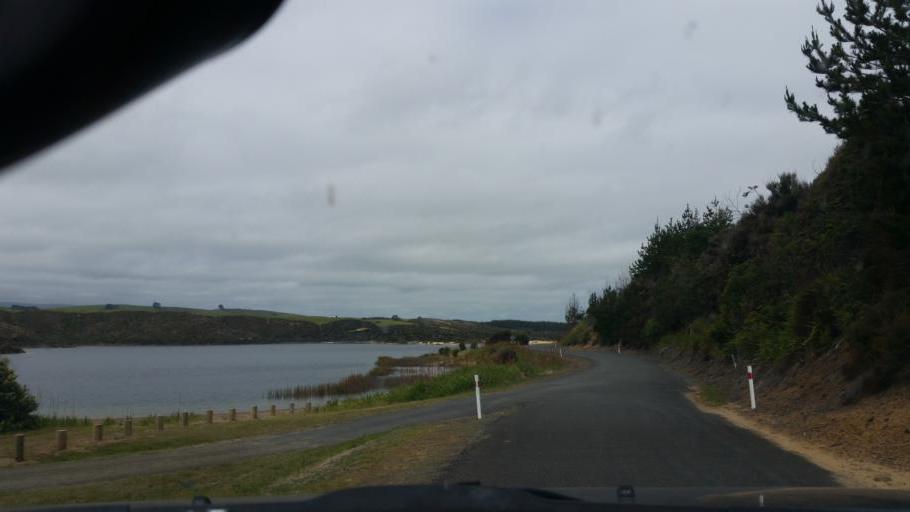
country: NZ
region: Northland
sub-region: Kaipara District
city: Dargaville
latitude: -35.7987
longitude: 173.6255
